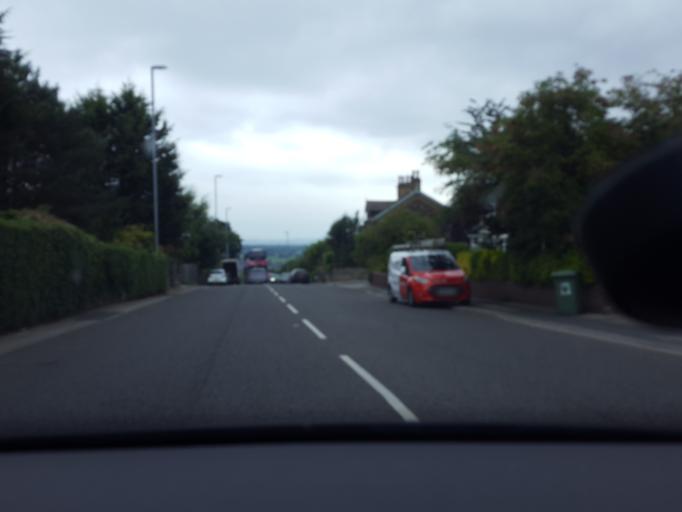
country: GB
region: England
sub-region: City and Borough of Leeds
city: Horsforth
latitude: 53.8152
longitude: -1.6364
